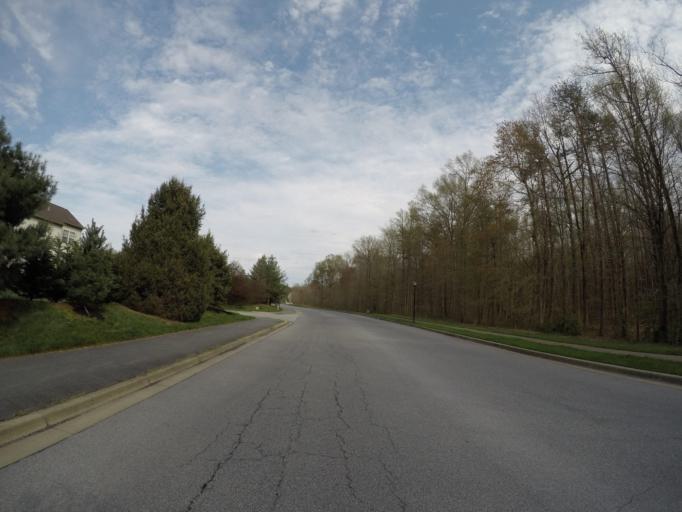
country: US
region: Delaware
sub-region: New Castle County
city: Glasgow
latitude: 39.5613
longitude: -75.7585
